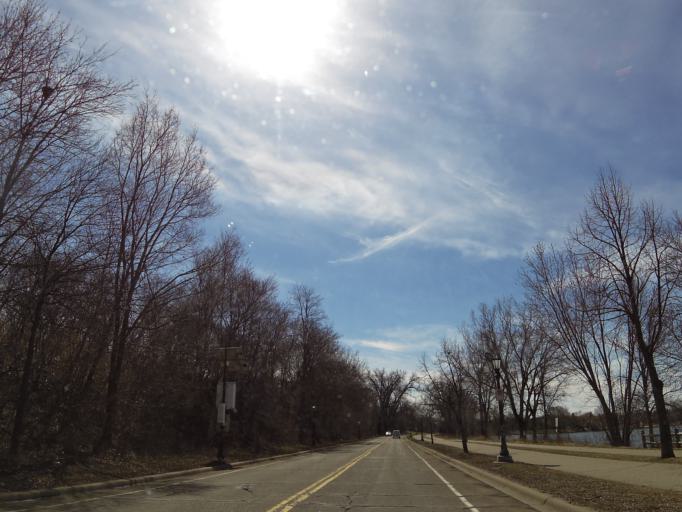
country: US
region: Minnesota
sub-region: Ramsey County
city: Maplewood
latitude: 44.9826
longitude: -93.0457
